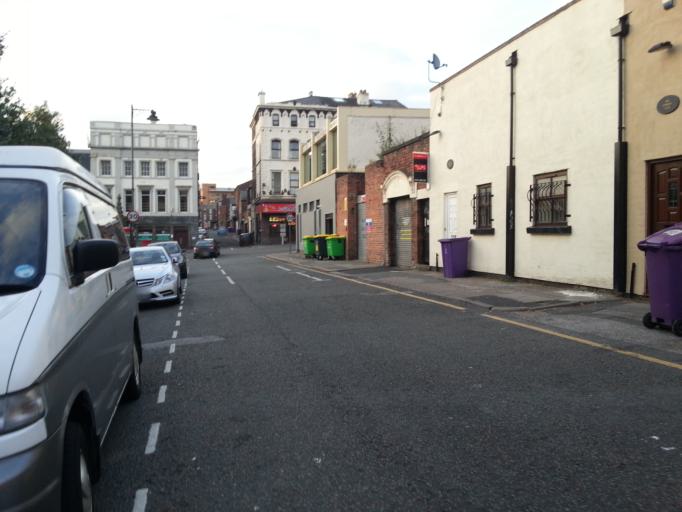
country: GB
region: England
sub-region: Liverpool
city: Liverpool
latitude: 53.4016
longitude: -2.9743
